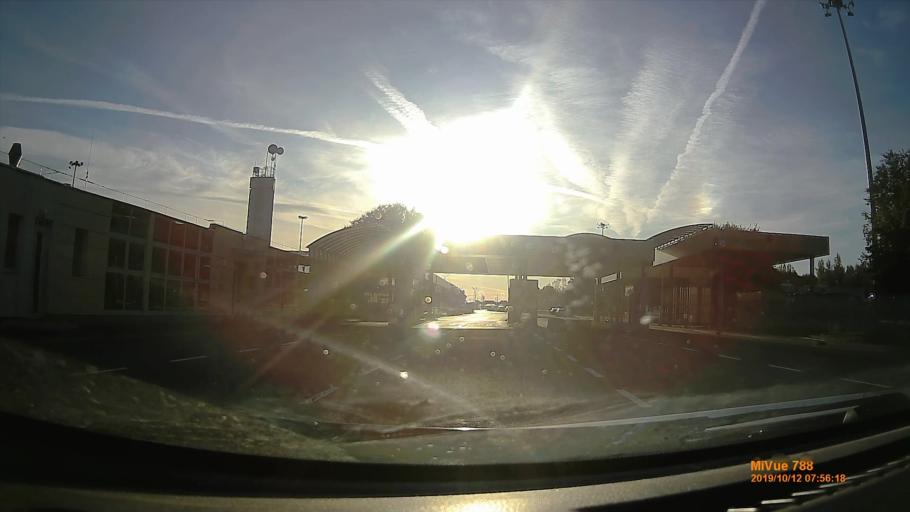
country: RO
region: Bihor
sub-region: Comuna Bors
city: Bors
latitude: 47.1194
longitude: 21.7885
